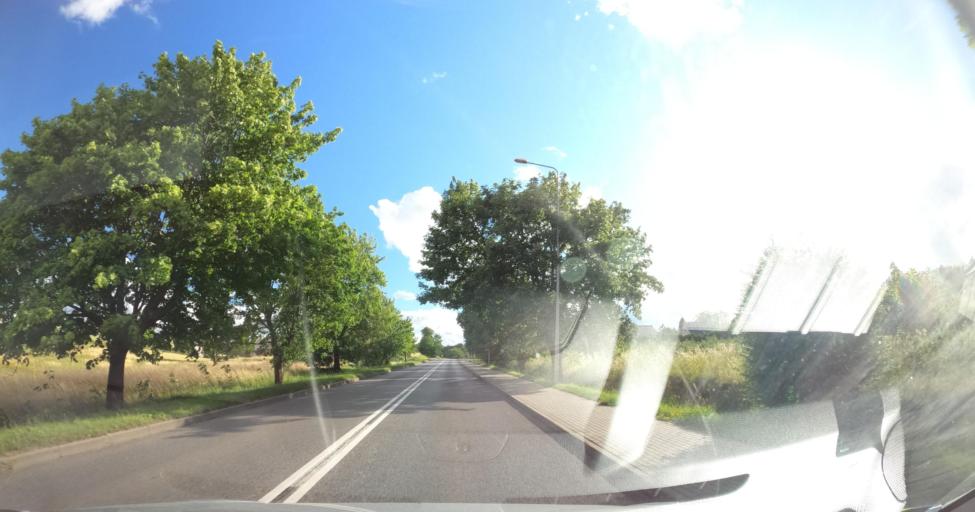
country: PL
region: Pomeranian Voivodeship
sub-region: Powiat kartuski
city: Zukowo
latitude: 54.3305
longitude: 18.3286
